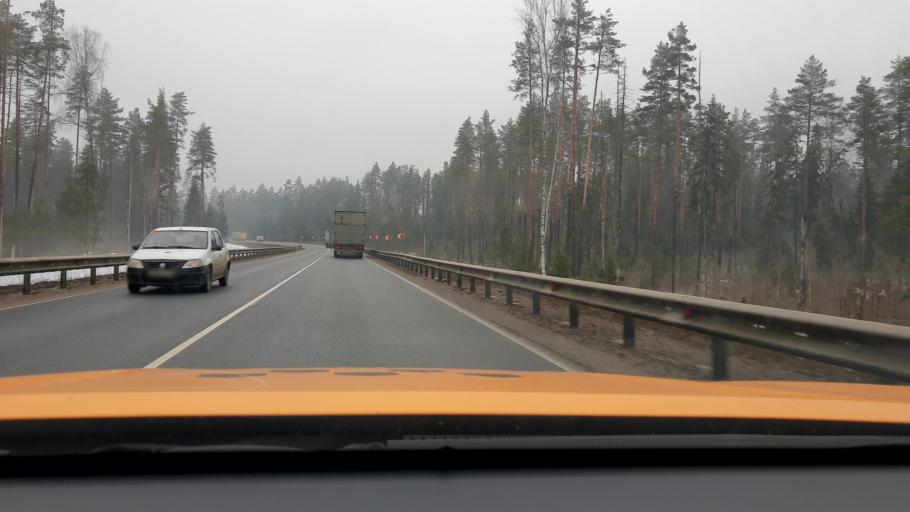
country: RU
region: Moskovskaya
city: Chernogolovka
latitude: 56.0034
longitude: 38.2943
